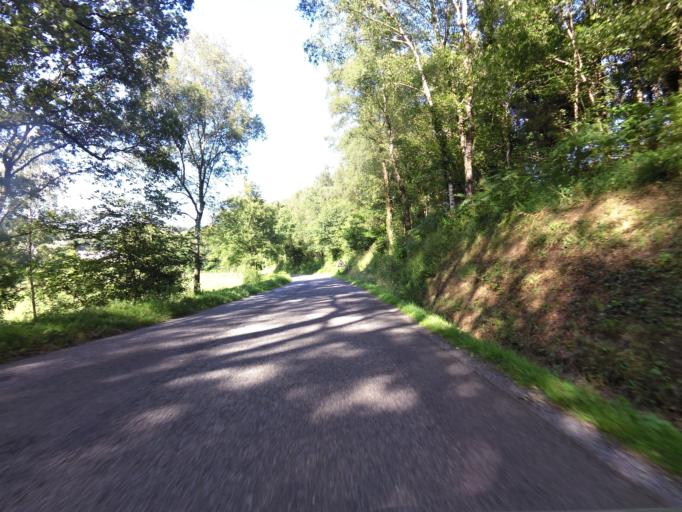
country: FR
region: Brittany
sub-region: Departement du Morbihan
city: Limerzel
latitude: 47.6303
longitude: -2.3411
